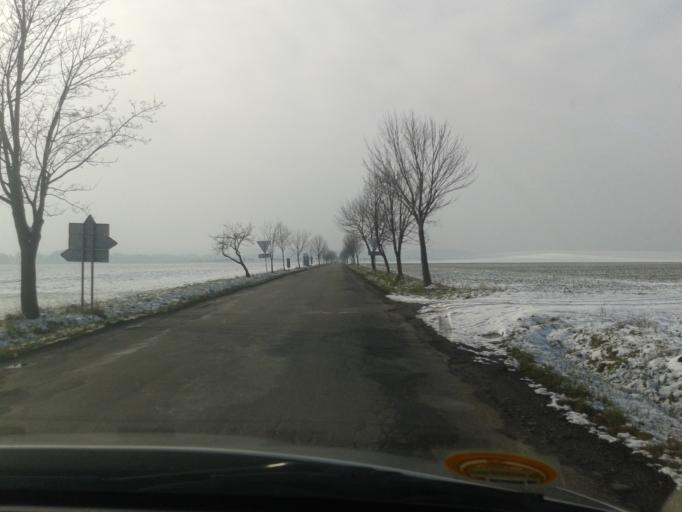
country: CZ
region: Olomoucky
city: Celechovice na Hane
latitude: 49.4924
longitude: 17.0823
